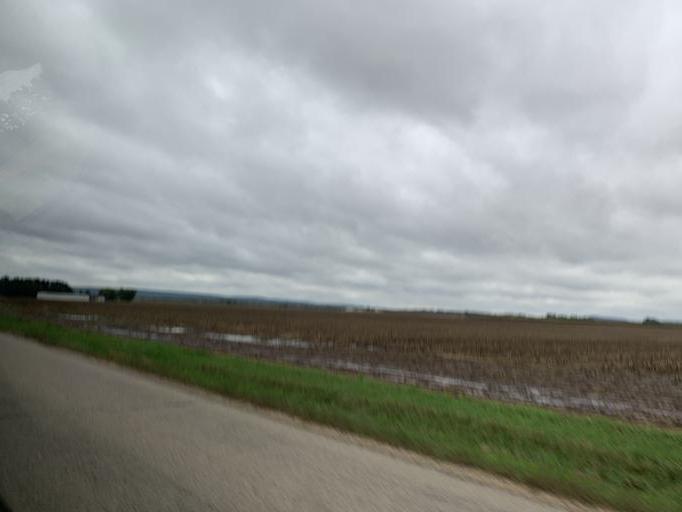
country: US
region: Wisconsin
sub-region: Sauk County
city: Prairie du Sac
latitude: 43.3087
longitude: -89.7789
